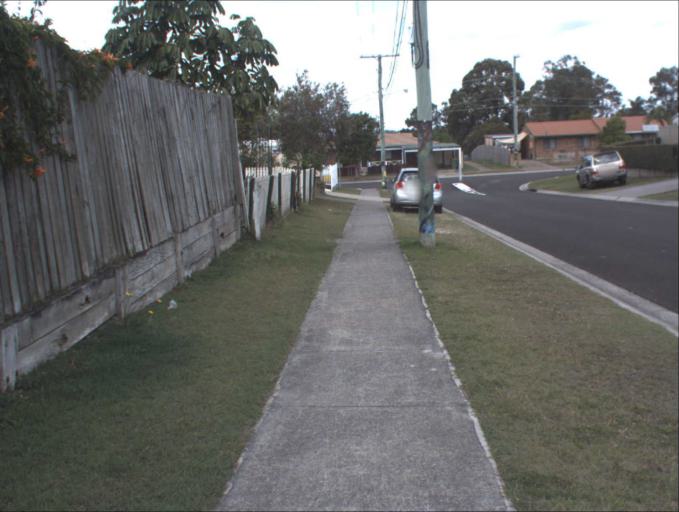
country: AU
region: Queensland
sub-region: Logan
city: Logan Reserve
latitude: -27.6857
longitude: 153.0892
